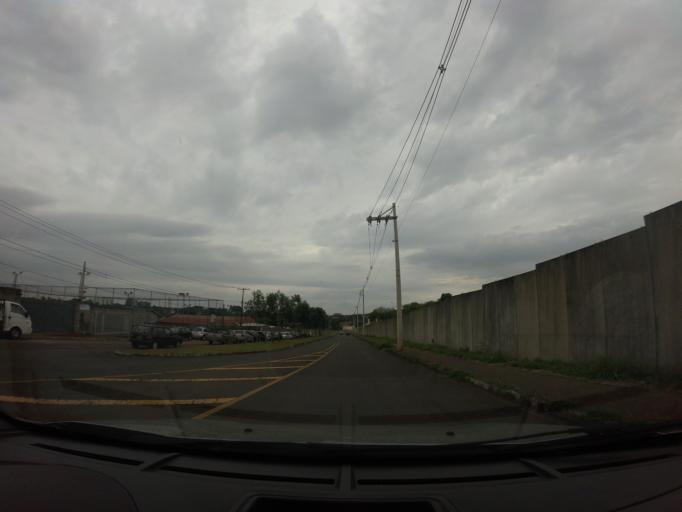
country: BR
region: Sao Paulo
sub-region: Piracicaba
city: Piracicaba
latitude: -22.7517
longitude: -47.5938
